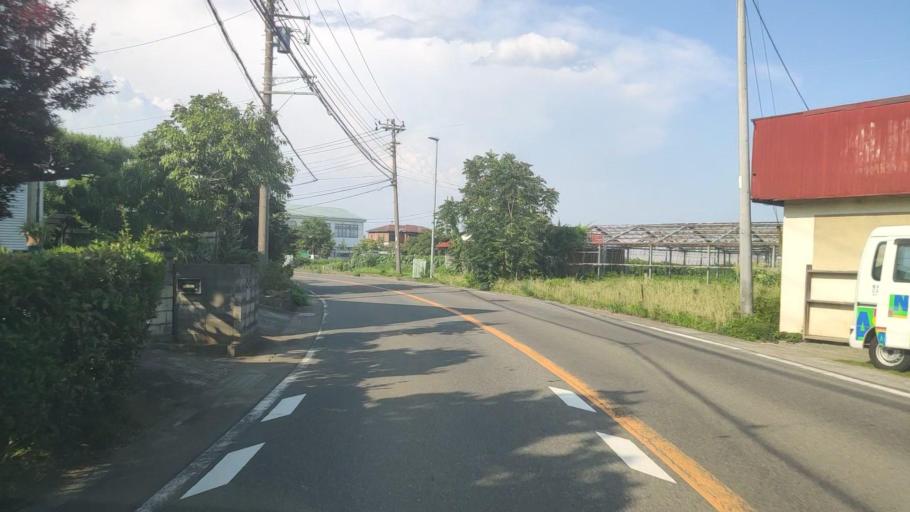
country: JP
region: Kanagawa
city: Isehara
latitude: 35.3721
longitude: 139.3321
